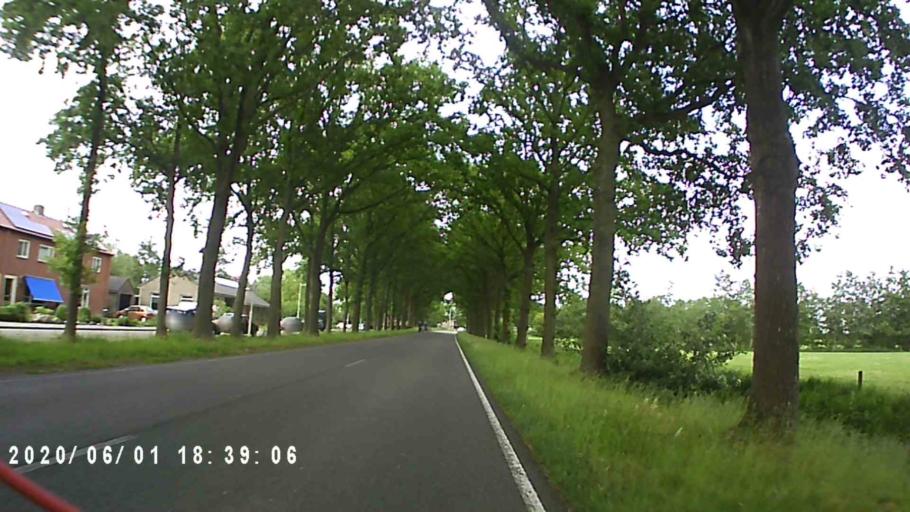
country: NL
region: Friesland
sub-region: Gemeente Tytsjerksteradiel
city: Eastermar
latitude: 53.1737
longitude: 6.0600
